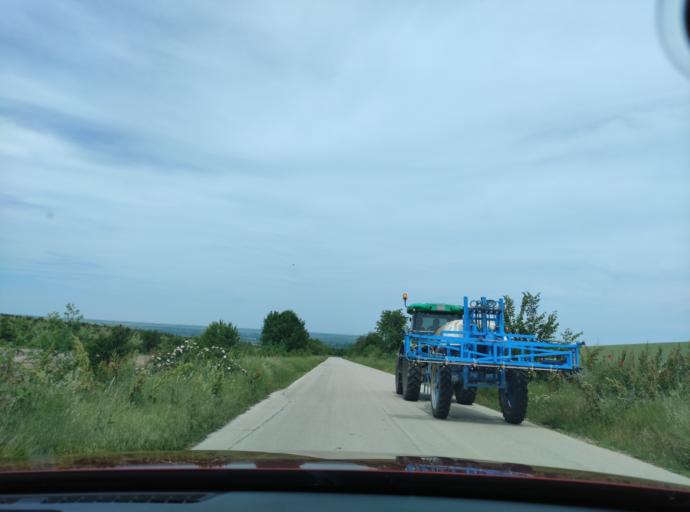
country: BG
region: Pleven
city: Iskur
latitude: 43.5305
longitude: 24.3059
